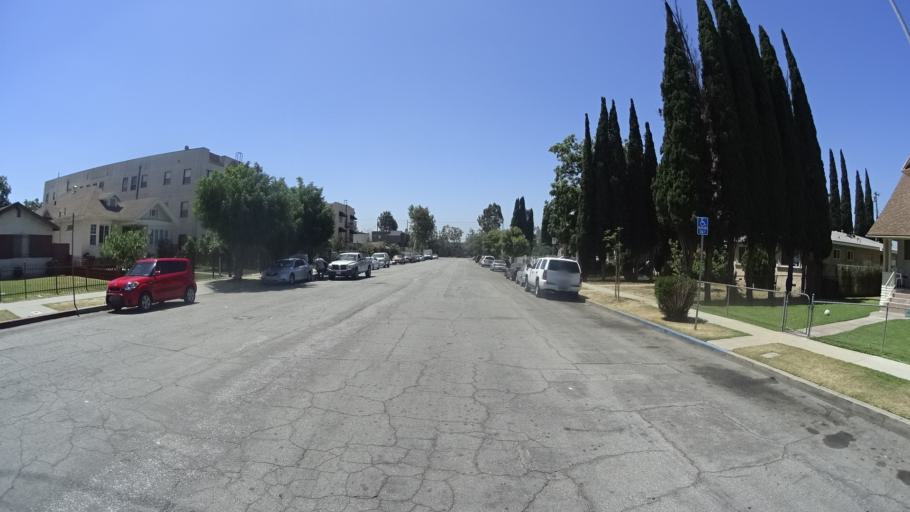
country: US
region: California
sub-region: Los Angeles County
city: View Park-Windsor Hills
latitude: 34.0273
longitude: -118.3028
